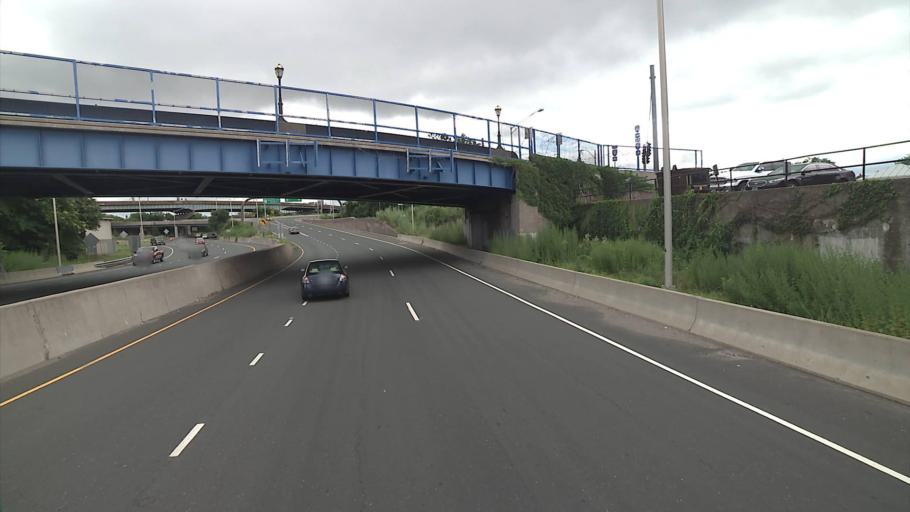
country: US
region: Connecticut
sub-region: Hartford County
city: Hartford
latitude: 41.7607
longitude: -72.6684
